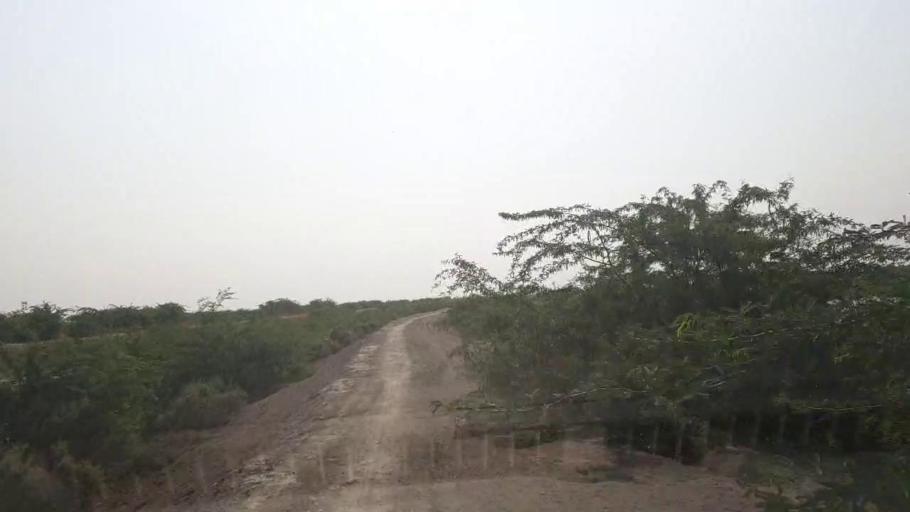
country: PK
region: Sindh
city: Kadhan
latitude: 24.3926
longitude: 68.9030
